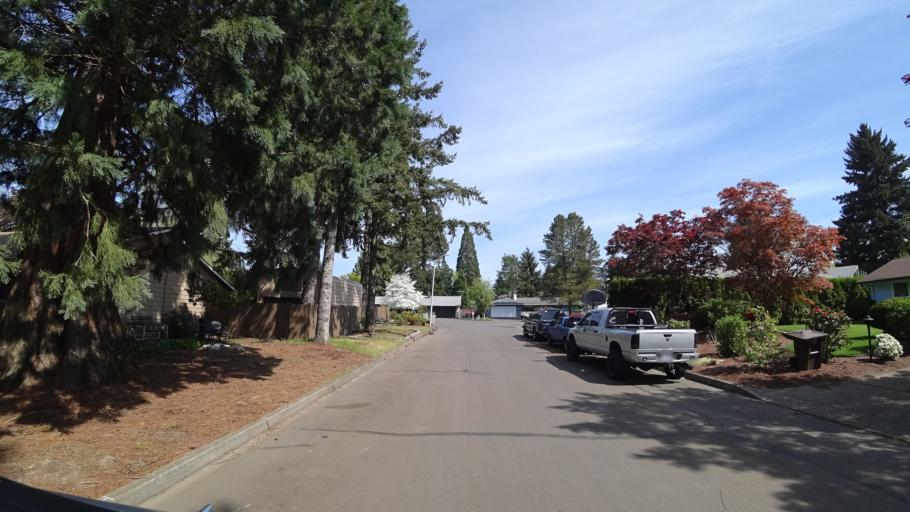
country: US
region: Oregon
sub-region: Washington County
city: Hillsboro
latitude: 45.5147
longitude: -122.9445
